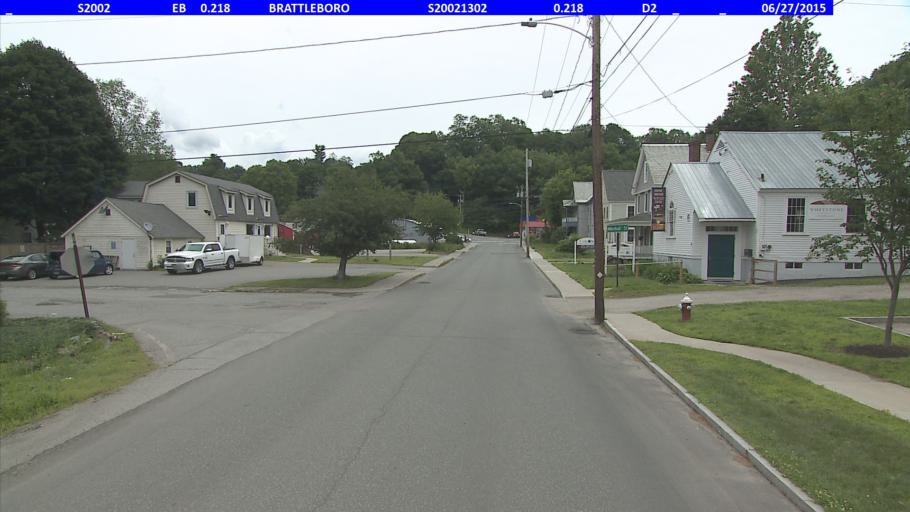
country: US
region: Vermont
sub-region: Windham County
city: Brattleboro
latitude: 42.8463
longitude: -72.5645
